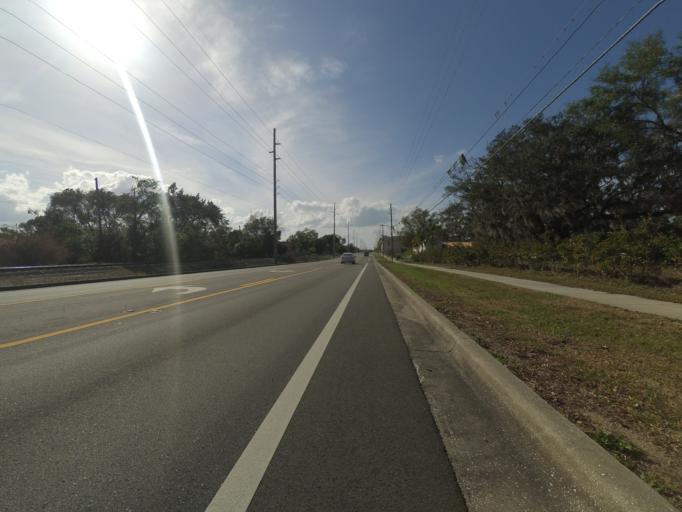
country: US
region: Florida
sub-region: Lake County
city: Mount Dora
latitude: 28.8073
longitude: -81.6631
